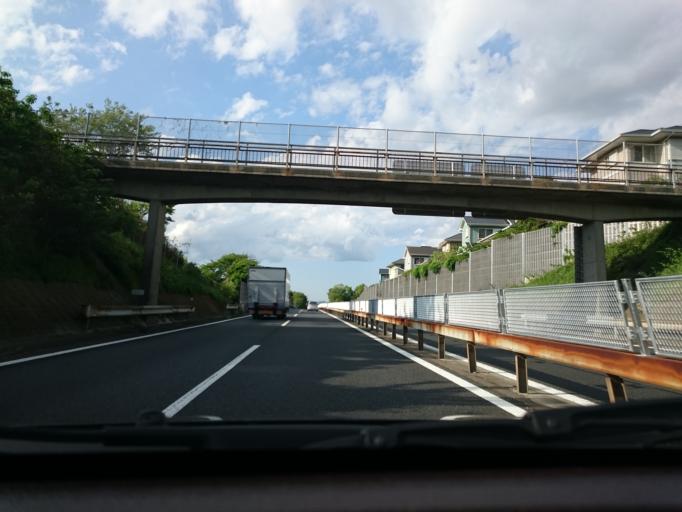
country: JP
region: Kanagawa
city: Oiso
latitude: 35.3419
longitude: 139.2965
